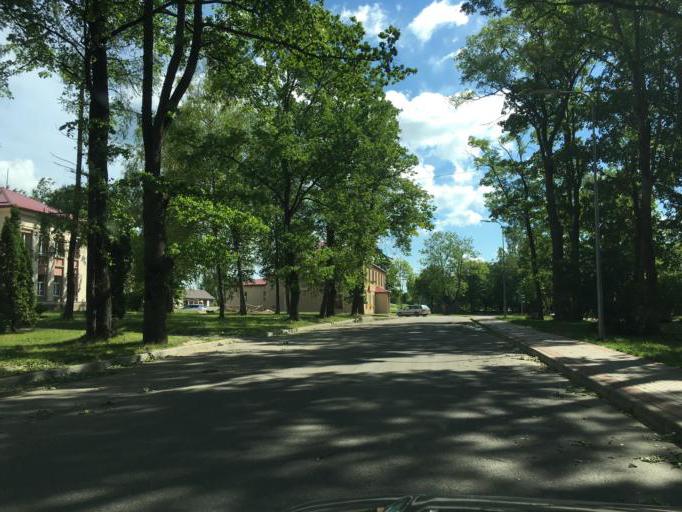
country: LV
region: Balvu Rajons
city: Balvi
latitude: 57.1393
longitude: 27.2556
